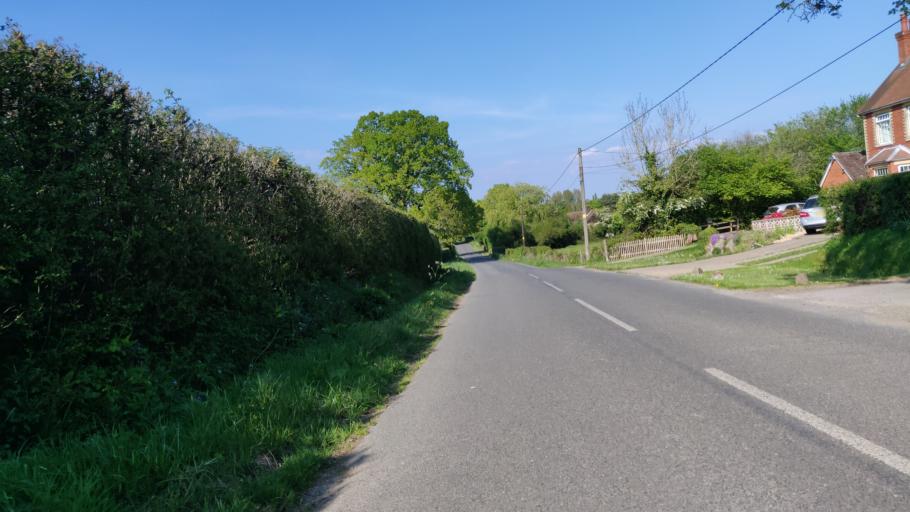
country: GB
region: England
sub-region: West Sussex
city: Southwater
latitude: 51.0427
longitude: -0.3563
